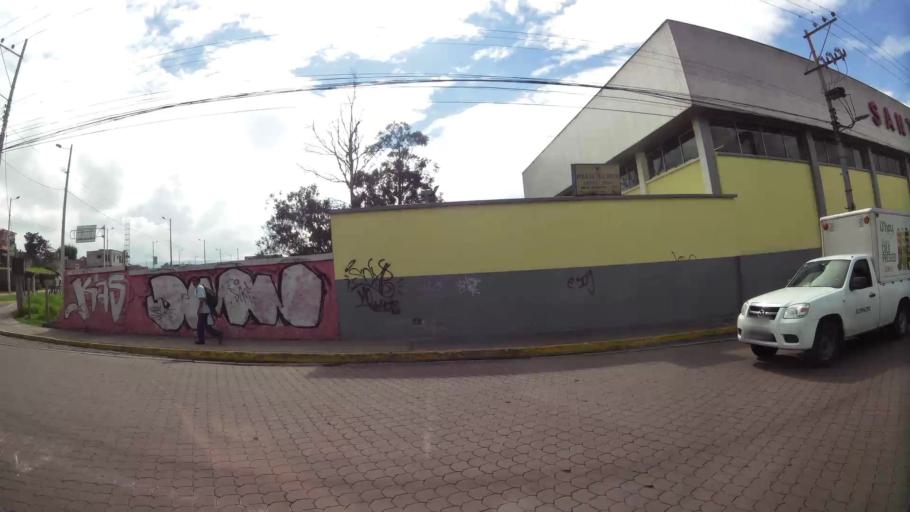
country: EC
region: Pichincha
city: Sangolqui
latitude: -0.3300
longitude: -78.4513
